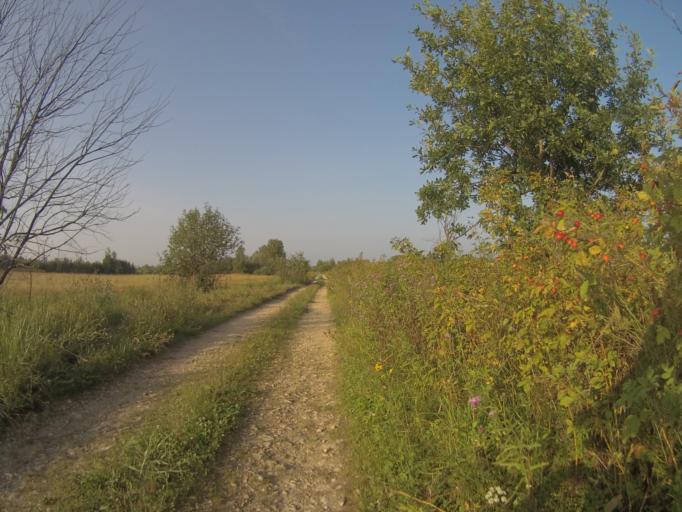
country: RU
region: Vladimir
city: Kommunar
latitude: 56.1194
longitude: 40.4464
